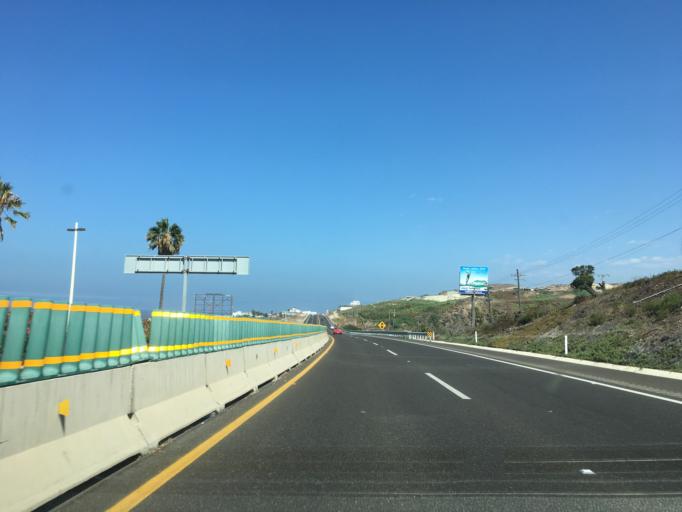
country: MX
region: Baja California
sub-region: Tijuana
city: La Esperanza [Granjas Familiares]
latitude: 32.4458
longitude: -117.1034
